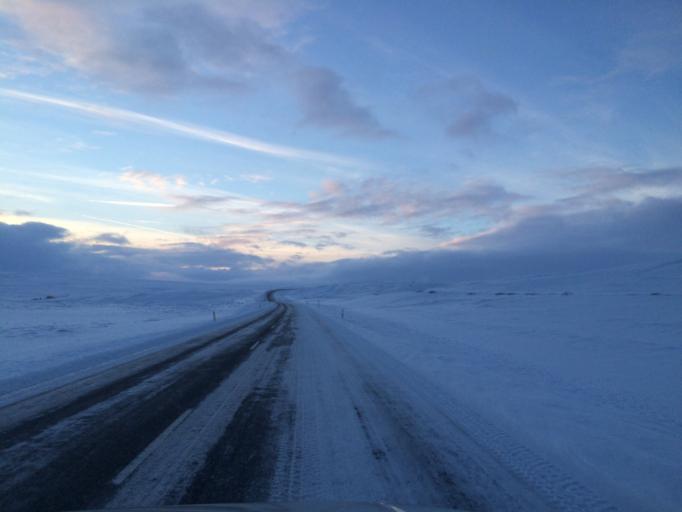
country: IS
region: South
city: Hveragerdi
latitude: 64.2277
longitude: -21.2065
